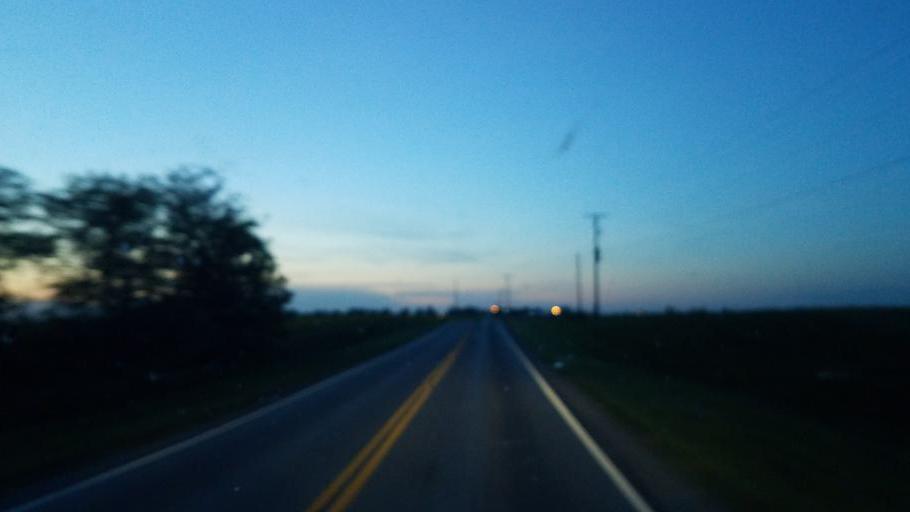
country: US
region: Ohio
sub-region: Highland County
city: Greenfield
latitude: 39.2500
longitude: -83.4402
